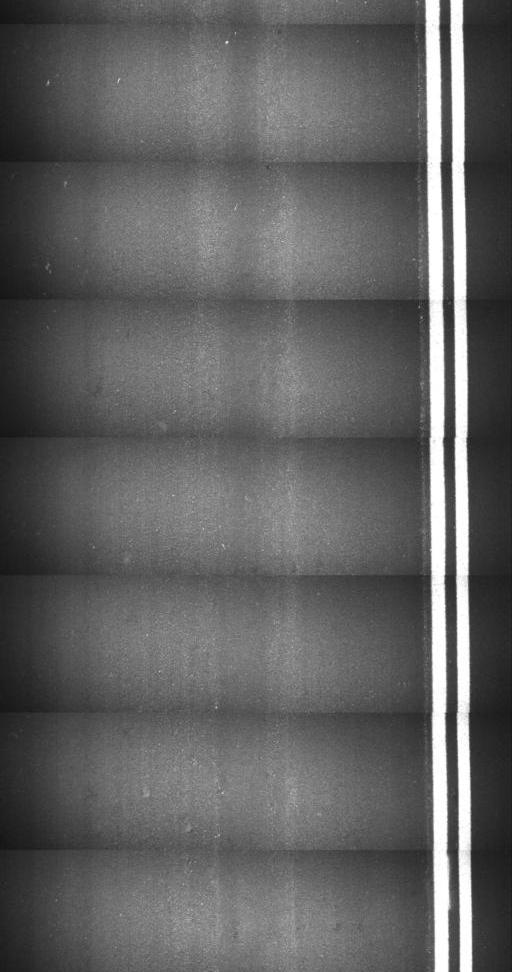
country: US
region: Vermont
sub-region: Windsor County
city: Woodstock
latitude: 43.5927
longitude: -72.5170
